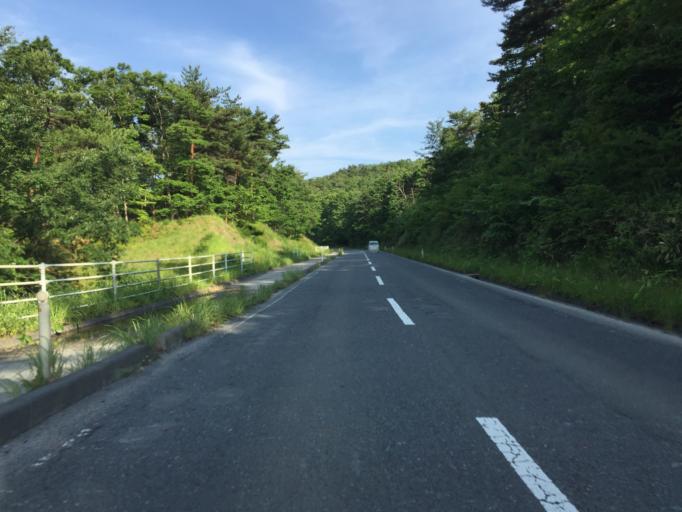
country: JP
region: Fukushima
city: Namie
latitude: 37.6677
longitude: 140.9734
